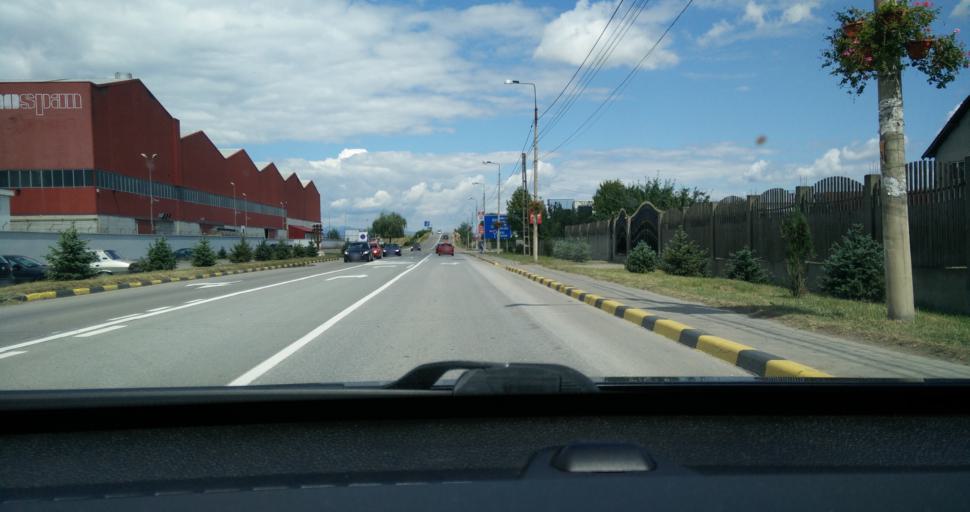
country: RO
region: Alba
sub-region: Municipiul Sebes
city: Sebes
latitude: 45.9687
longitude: 23.5576
